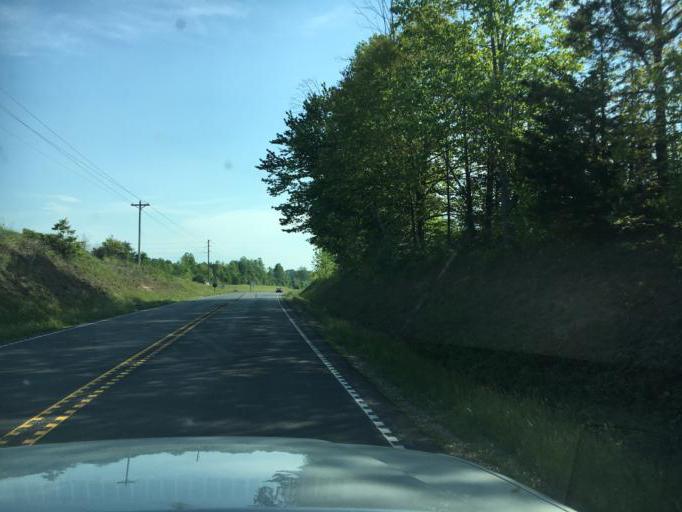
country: US
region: North Carolina
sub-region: Burke County
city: Glen Alpine
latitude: 35.6356
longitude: -81.7954
